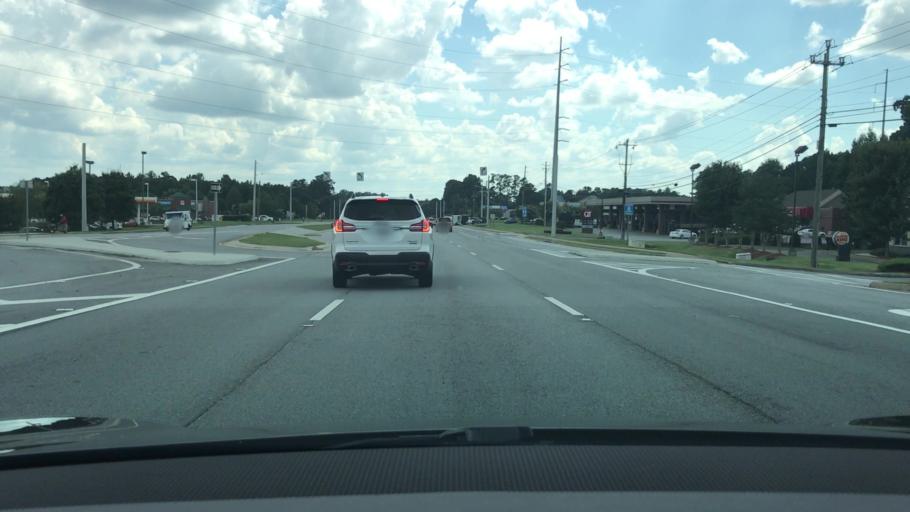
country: US
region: Georgia
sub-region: Gwinnett County
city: Suwanee
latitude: 34.0521
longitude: -84.0907
